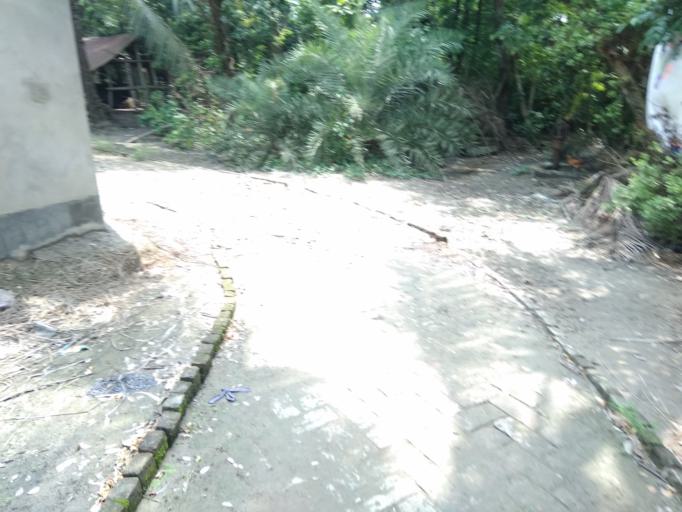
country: BD
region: Chittagong
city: Chhagalnaiya
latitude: 22.8186
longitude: 91.4943
